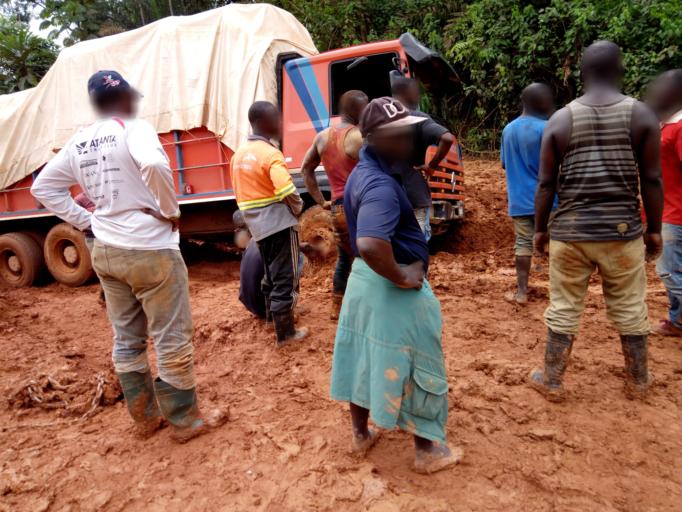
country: LR
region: Grand Gedeh
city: Zwedru
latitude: 6.1914
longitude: -8.3230
